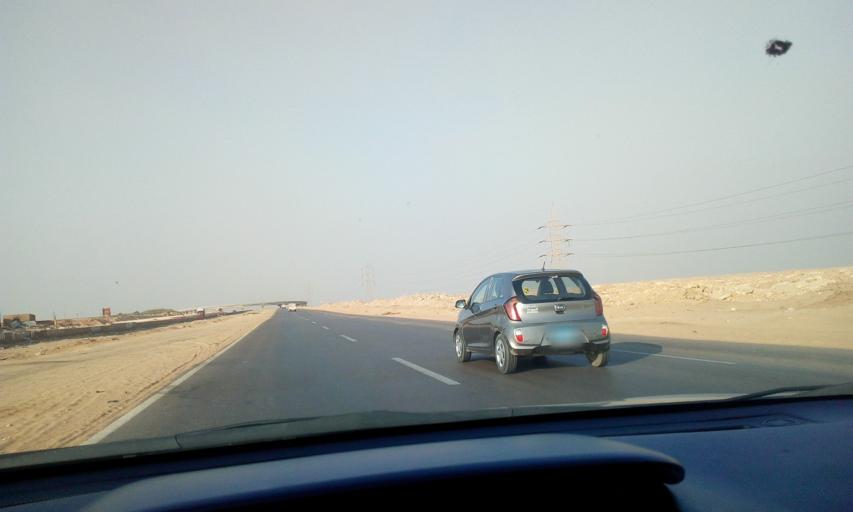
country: EG
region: Al Jizah
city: Madinat Sittah Uktubar
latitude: 29.9187
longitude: 31.0933
